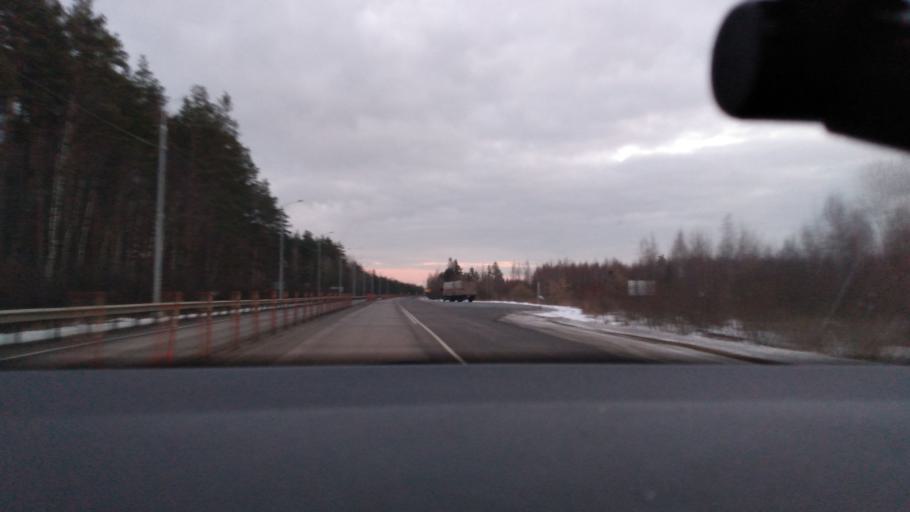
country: RU
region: Moskovskaya
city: Yegor'yevsk
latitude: 55.4488
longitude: 39.0081
